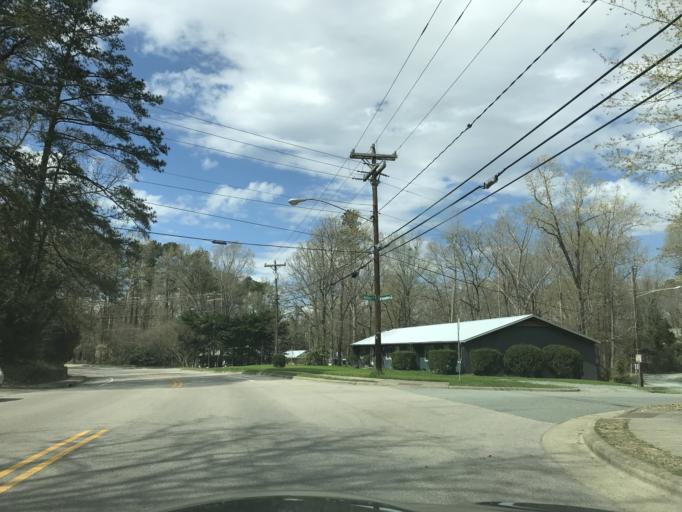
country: US
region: North Carolina
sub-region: Orange County
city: Carrboro
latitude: 35.9201
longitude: -79.0782
